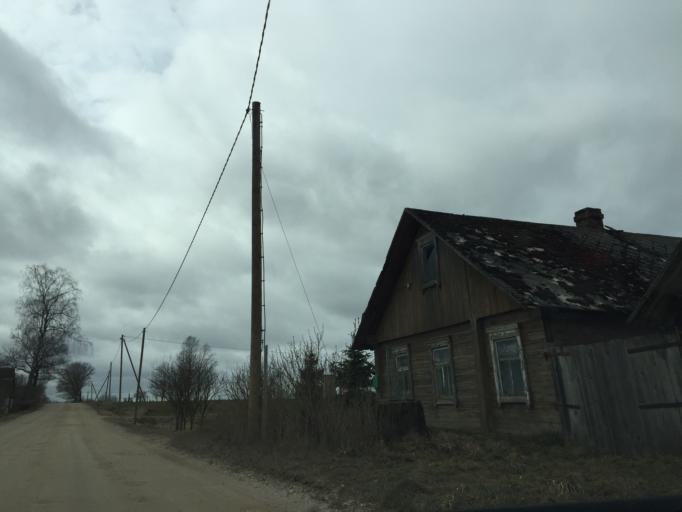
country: LV
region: Kraslavas Rajons
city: Kraslava
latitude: 55.9426
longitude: 26.9798
